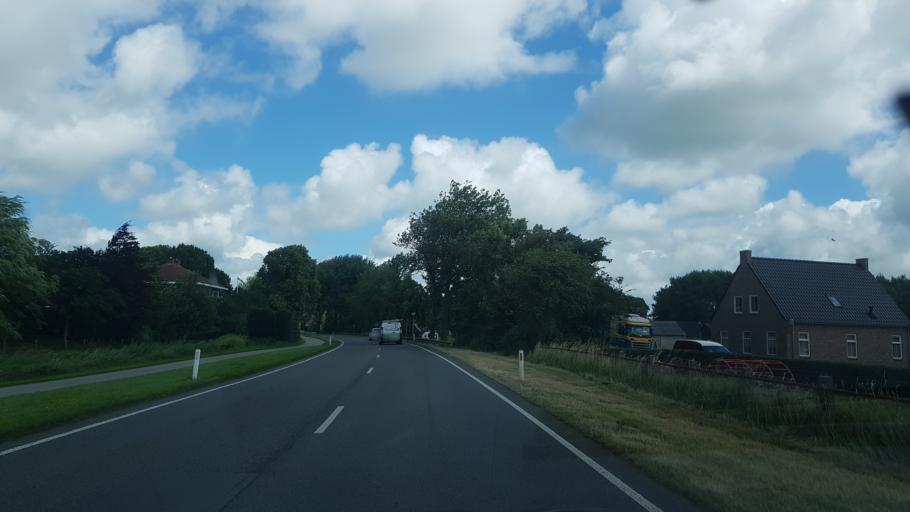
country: NL
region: Groningen
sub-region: Gemeente Bedum
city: Bedum
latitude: 53.4032
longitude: 6.6006
